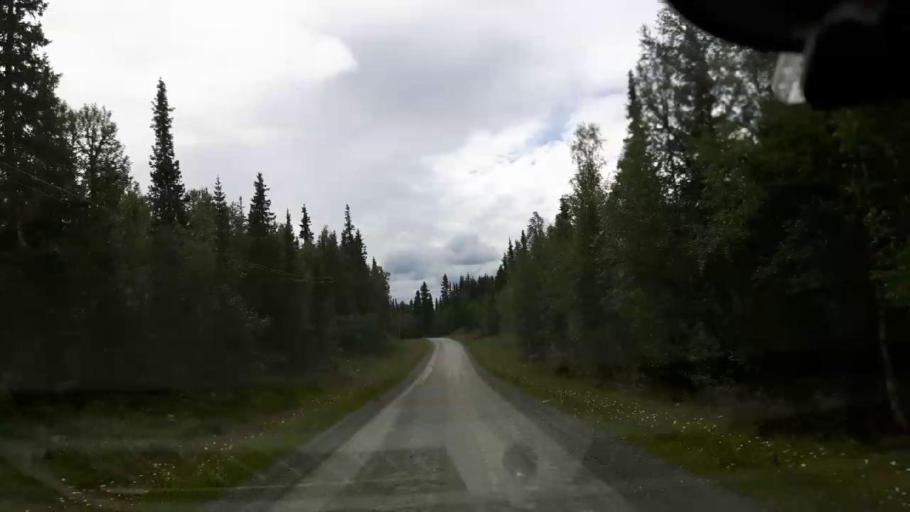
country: SE
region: Jaemtland
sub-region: Krokoms Kommun
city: Valla
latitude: 63.7335
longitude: 13.8361
